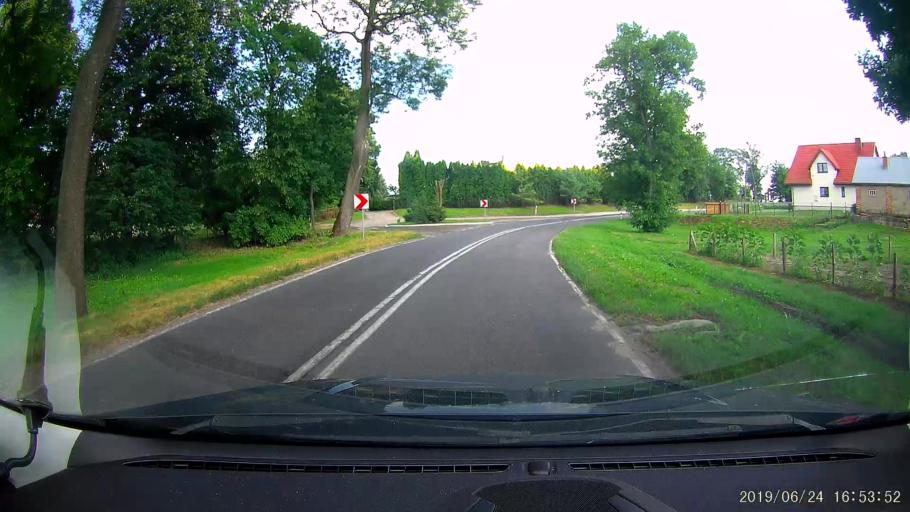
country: PL
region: Lublin Voivodeship
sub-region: Powiat tomaszowski
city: Telatyn
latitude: 50.5342
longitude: 23.8072
